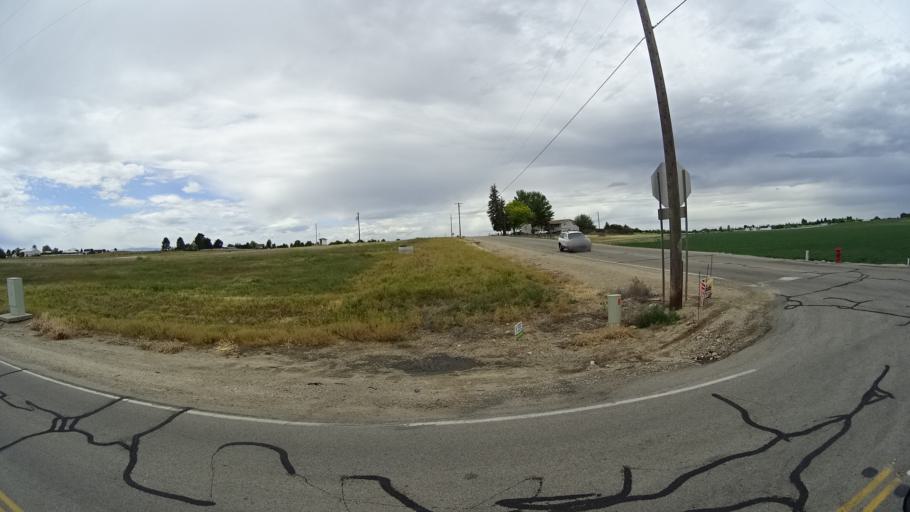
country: US
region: Idaho
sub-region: Ada County
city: Meridian
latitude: 43.5609
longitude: -116.4138
